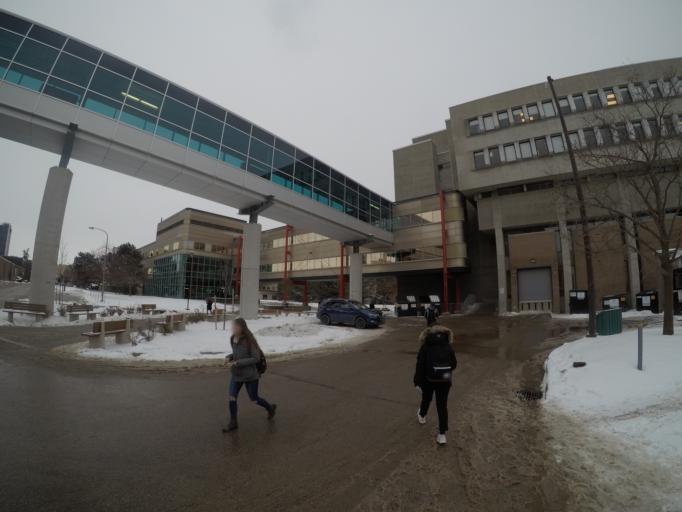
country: CA
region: Ontario
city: Waterloo
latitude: 43.4727
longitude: -80.5443
